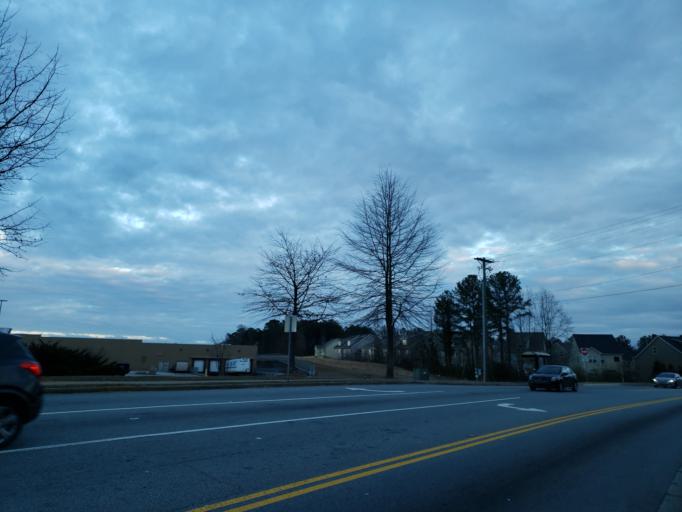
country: US
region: Georgia
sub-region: Cobb County
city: Mableton
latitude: 33.8553
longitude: -84.5893
